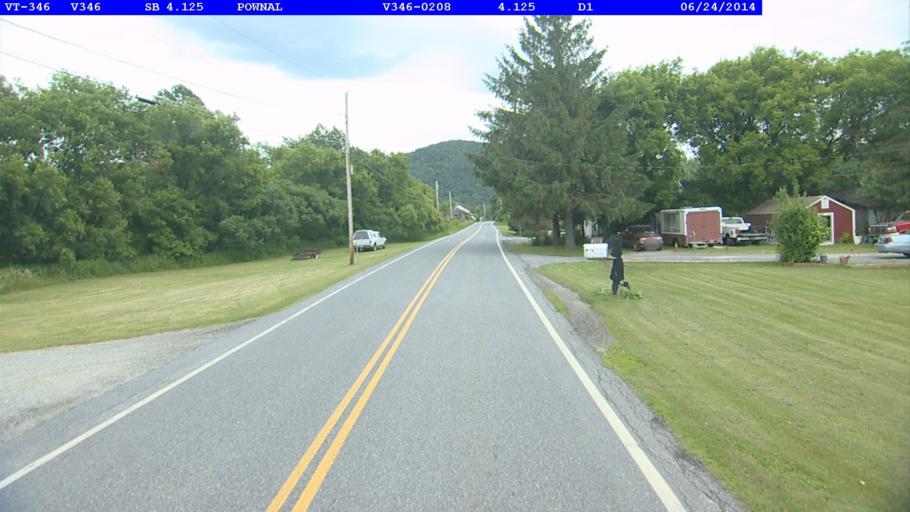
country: US
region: Vermont
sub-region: Bennington County
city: Bennington
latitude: 42.8079
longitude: -73.2768
